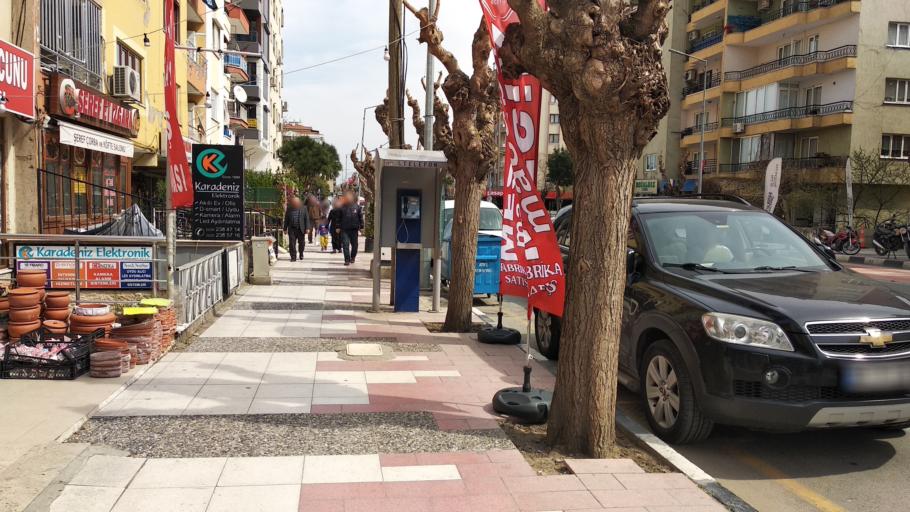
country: TR
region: Manisa
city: Manisa
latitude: 38.6126
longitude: 27.4118
